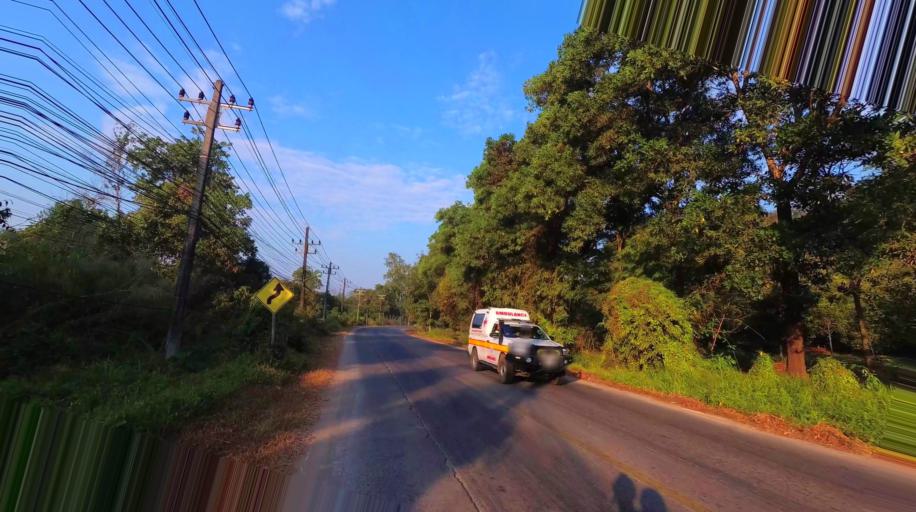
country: TH
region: Trat
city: Ko Chang Tai
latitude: 12.0586
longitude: 102.2957
